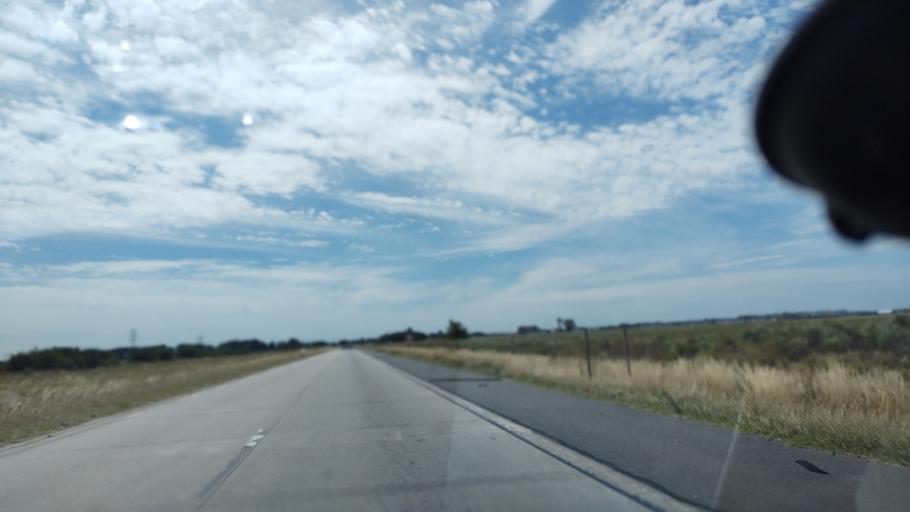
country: AR
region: Buenos Aires
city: Canuelas
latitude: -35.0665
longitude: -58.7012
